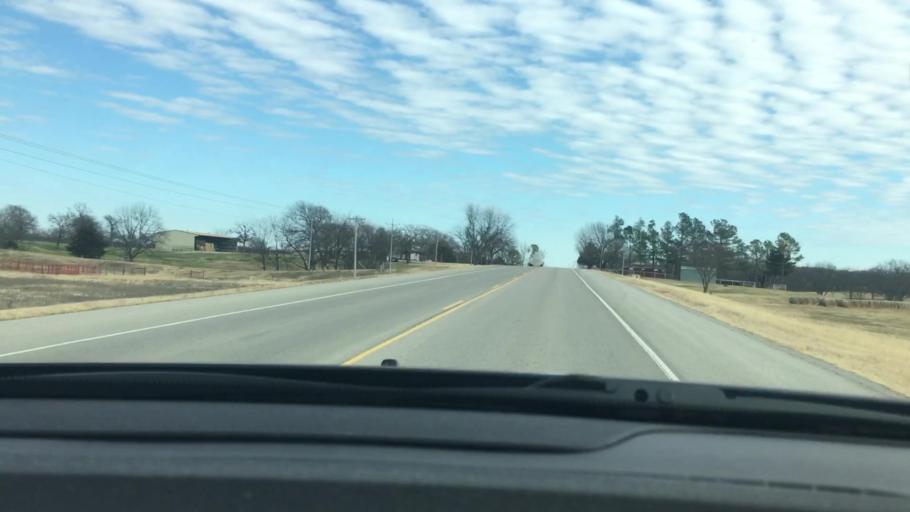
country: US
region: Oklahoma
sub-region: Garvin County
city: Pauls Valley
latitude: 34.7967
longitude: -97.1165
